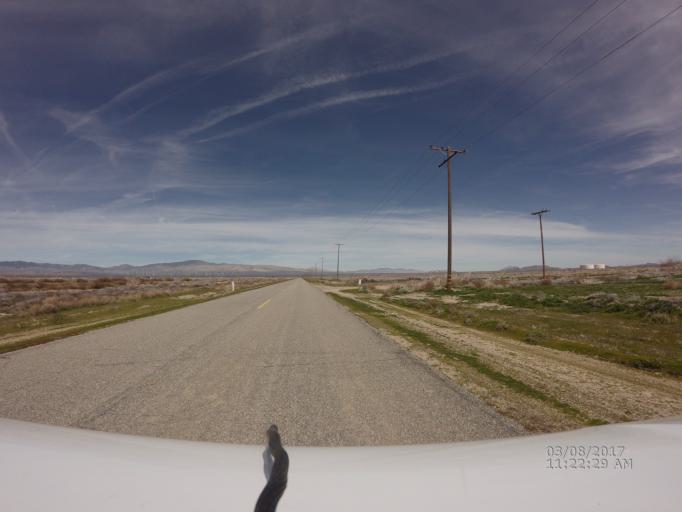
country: US
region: California
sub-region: Los Angeles County
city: Green Valley
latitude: 34.7983
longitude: -118.3790
